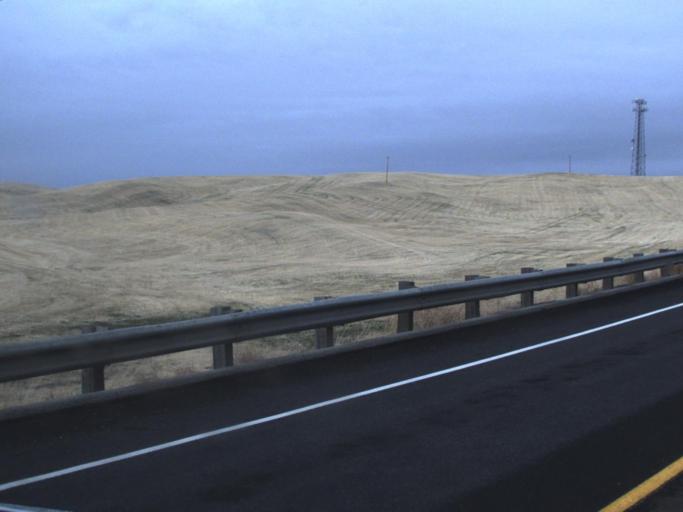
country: US
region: Washington
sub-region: Whitman County
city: Pullman
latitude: 46.6186
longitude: -117.1618
